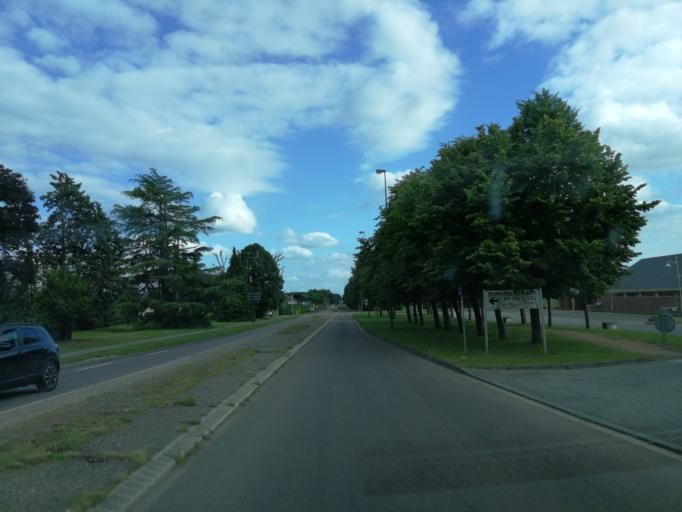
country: FR
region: Haute-Normandie
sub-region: Departement de l'Eure
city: Le Neubourg
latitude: 49.1413
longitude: 0.9033
